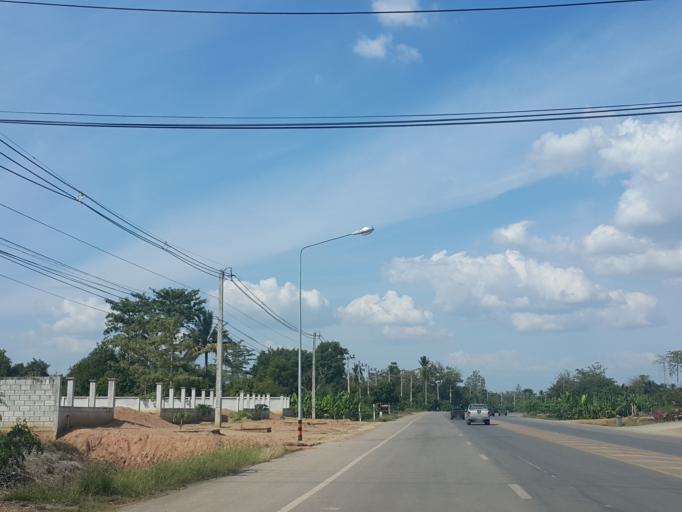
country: TH
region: Sukhothai
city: Si Samrong
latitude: 17.2310
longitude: 99.8468
